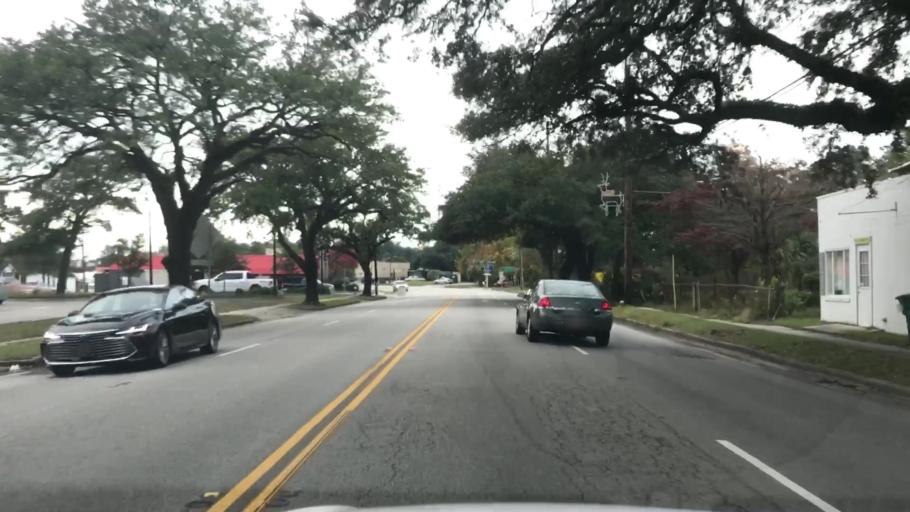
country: US
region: South Carolina
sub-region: Georgetown County
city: Georgetown
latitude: 33.3746
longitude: -79.2845
